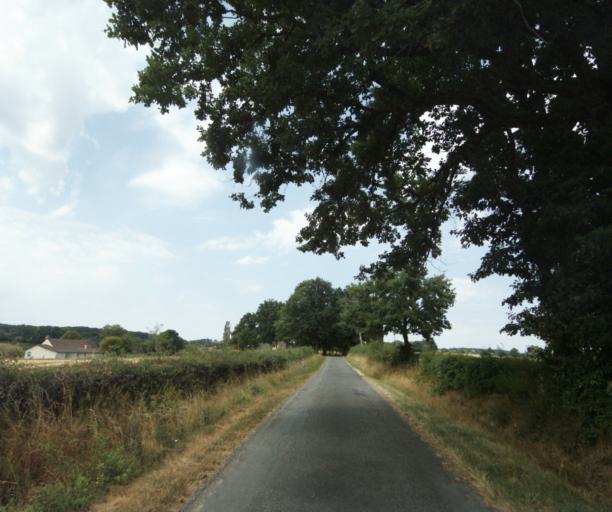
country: FR
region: Bourgogne
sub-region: Departement de Saone-et-Loire
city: Gueugnon
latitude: 46.5841
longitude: 4.0389
